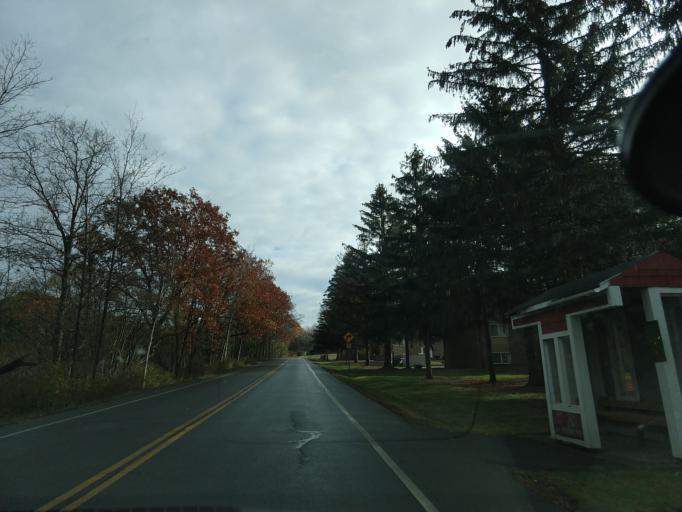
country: US
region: New York
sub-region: Tompkins County
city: Lansing
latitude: 42.4813
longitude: -76.4751
